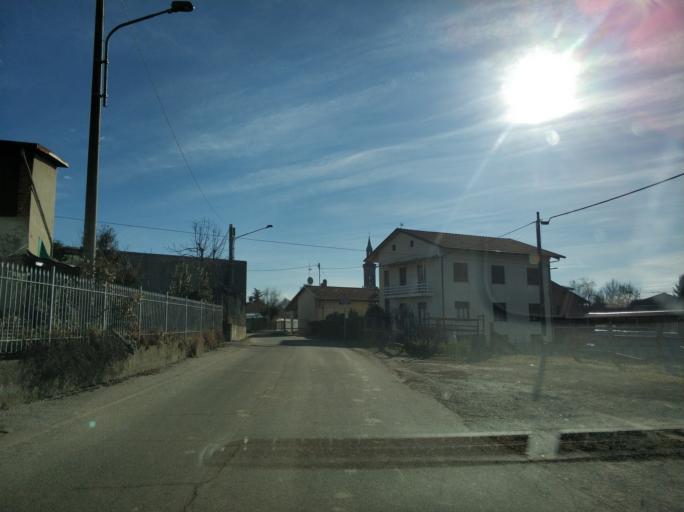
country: IT
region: Piedmont
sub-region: Provincia di Torino
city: San Carlo Canavese
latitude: 45.2508
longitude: 7.6082
